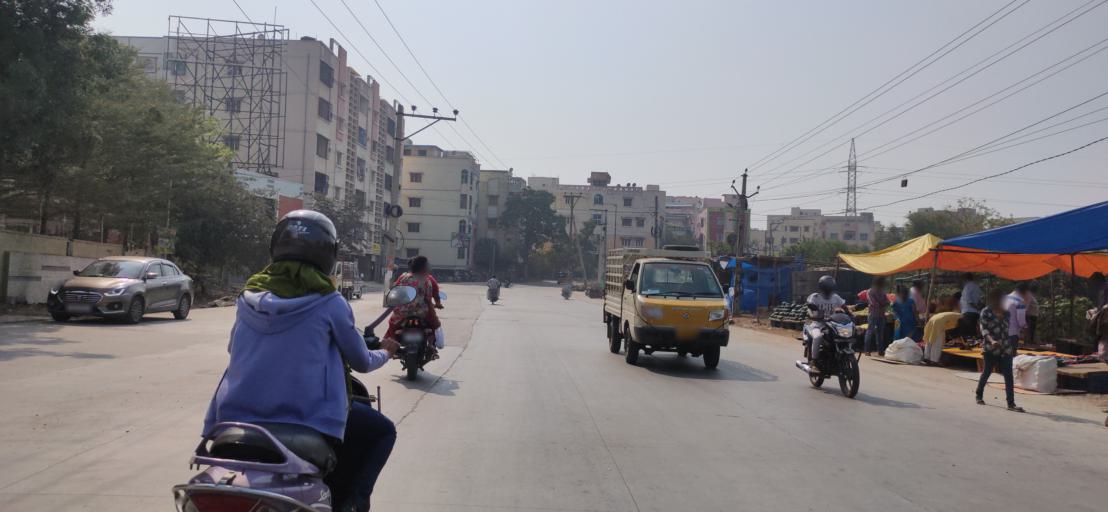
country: IN
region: Telangana
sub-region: Rangareddi
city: Kukatpalli
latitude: 17.5013
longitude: 78.4087
